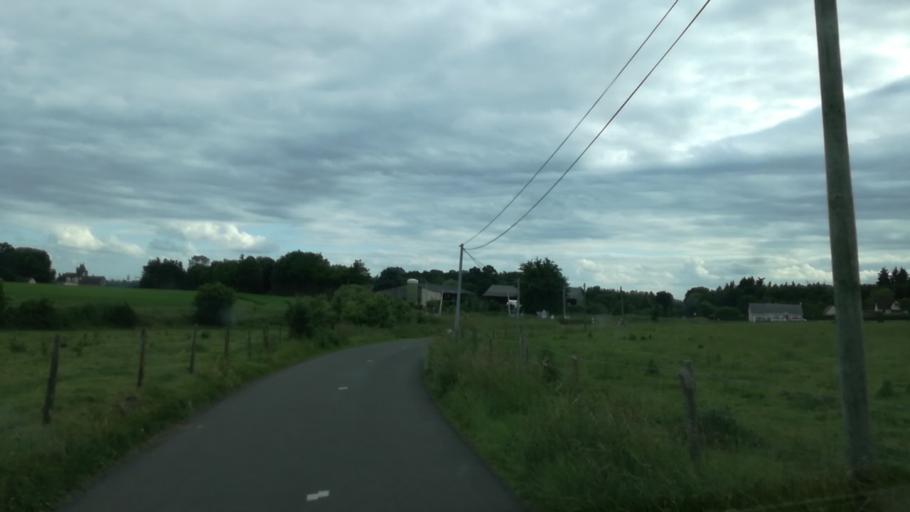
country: FR
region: Haute-Normandie
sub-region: Departement de l'Eure
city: Bourg-Achard
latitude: 49.2970
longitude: 0.8048
